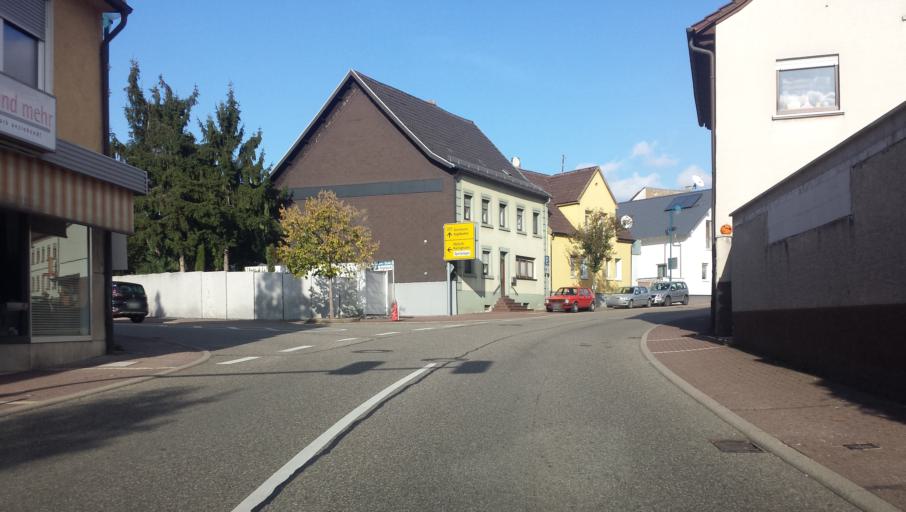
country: DE
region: Baden-Wuerttemberg
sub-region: Karlsruhe Region
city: Ostringen
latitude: 49.2200
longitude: 8.7131
